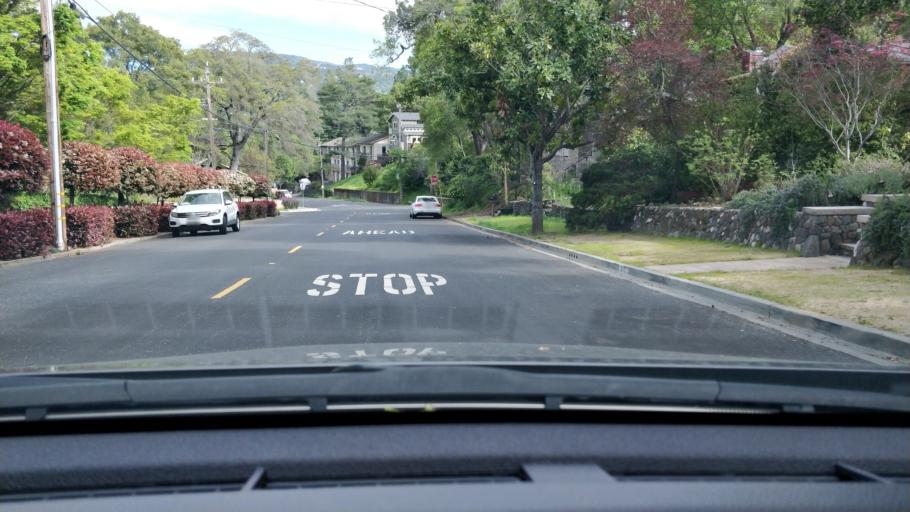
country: US
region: California
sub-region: Santa Clara County
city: Monte Sereno
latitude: 37.2258
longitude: -121.9897
